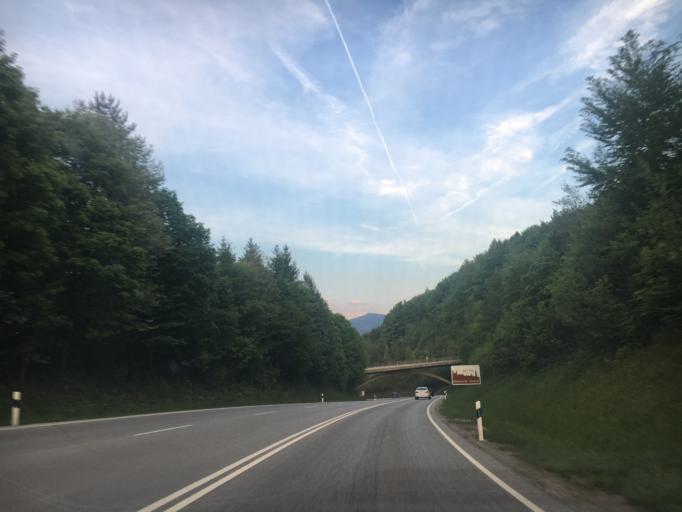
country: DE
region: Bavaria
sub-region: Upper Bavaria
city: Bad Toelz
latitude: 47.7555
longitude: 11.5456
